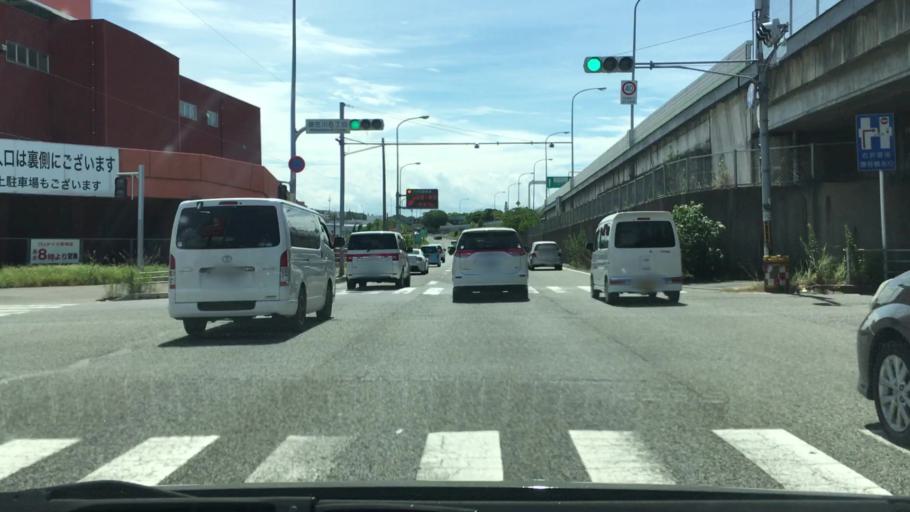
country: JP
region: Fukuoka
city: Onojo
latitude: 33.5339
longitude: 130.4896
